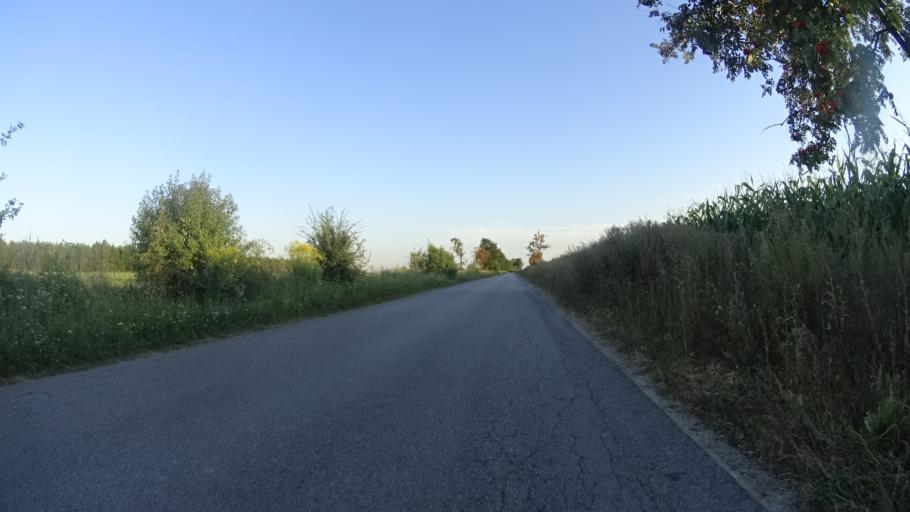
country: PL
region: Masovian Voivodeship
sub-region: Powiat bialobrzeski
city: Wysmierzyce
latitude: 51.6690
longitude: 20.8313
